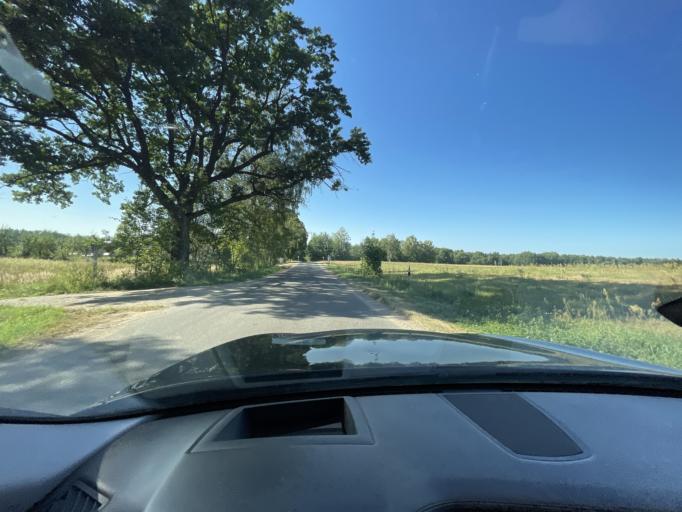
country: BY
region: Grodnenskaya
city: Hrodna
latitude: 53.7594
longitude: 23.9655
